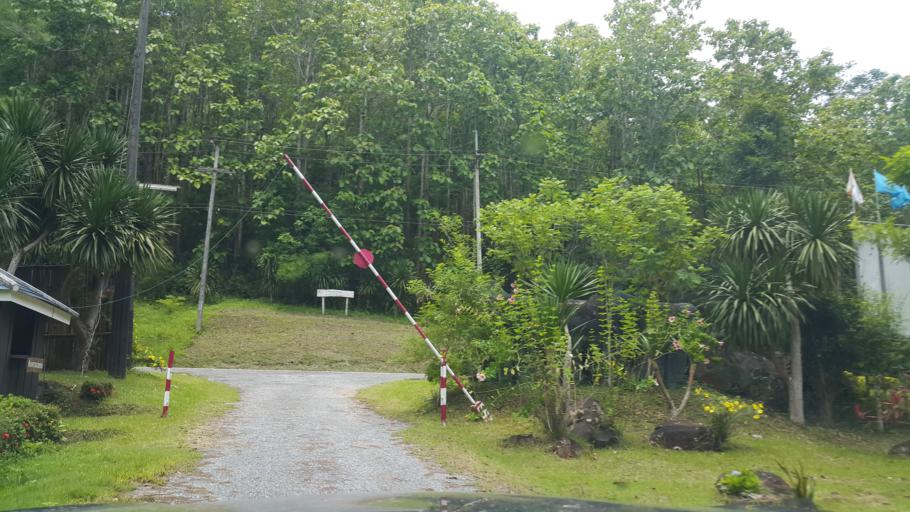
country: TH
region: Loei
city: Na Haeo
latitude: 17.6276
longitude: 100.8933
